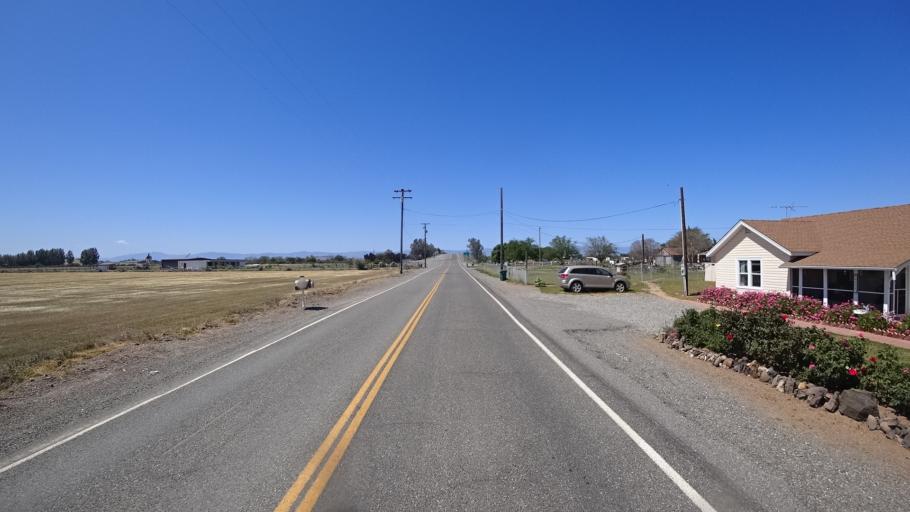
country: US
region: California
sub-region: Glenn County
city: Orland
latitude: 39.7836
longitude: -122.2004
